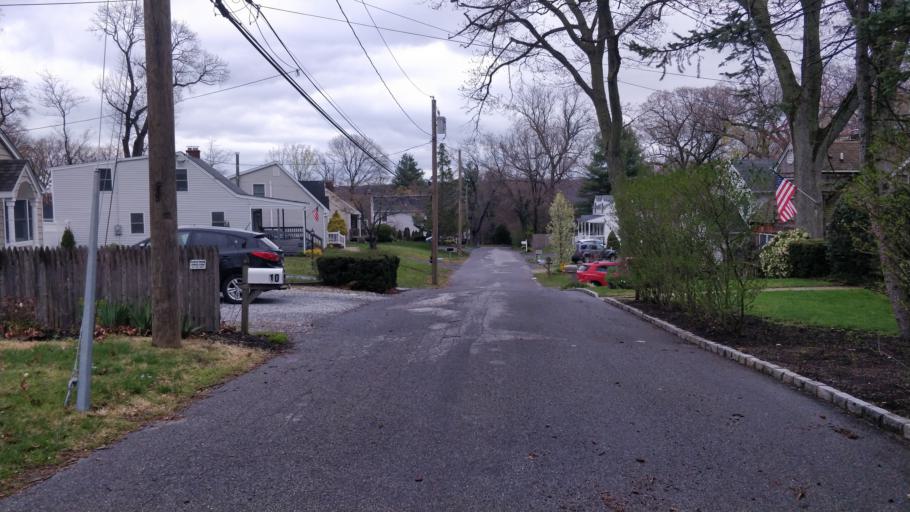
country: US
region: New York
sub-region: Suffolk County
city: Port Jefferson
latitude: 40.9501
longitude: -73.0811
